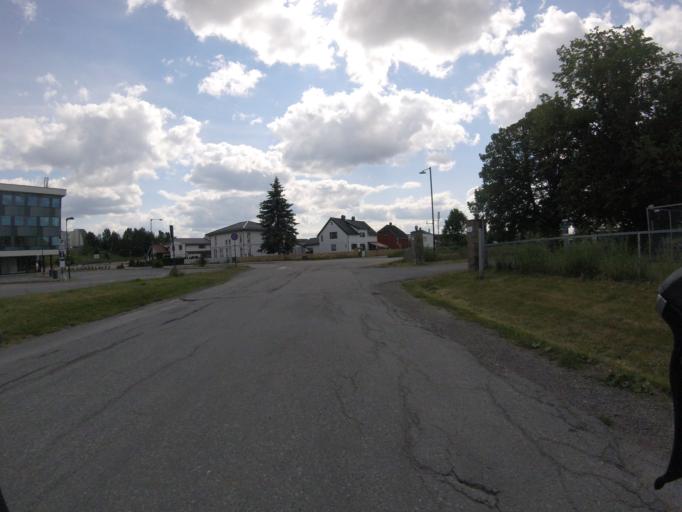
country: NO
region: Akershus
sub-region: Skedsmo
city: Lillestrom
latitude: 59.9742
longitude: 11.0464
